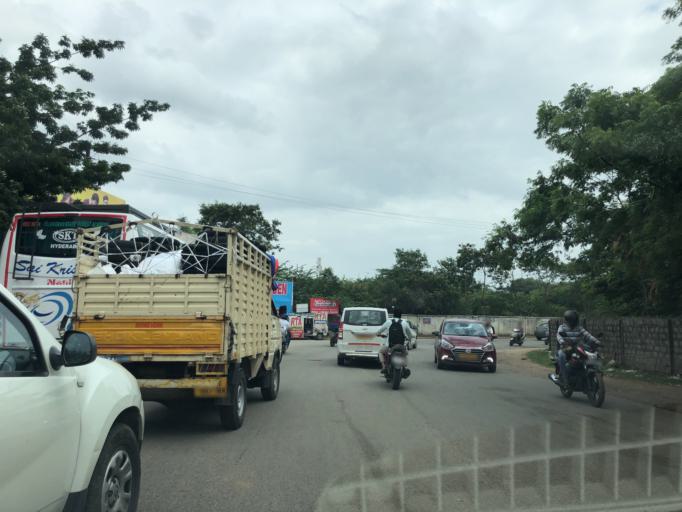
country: IN
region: Telangana
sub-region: Rangareddi
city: Quthbullapur
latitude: 17.4709
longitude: 78.4762
